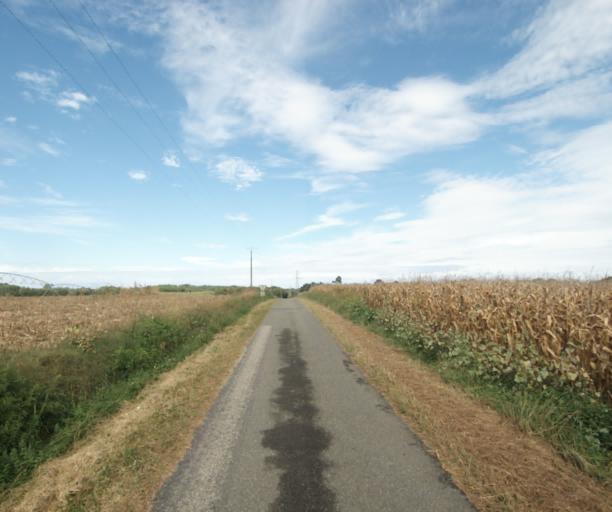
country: FR
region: Aquitaine
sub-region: Departement des Landes
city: Villeneuve-de-Marsan
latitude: 43.9011
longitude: -0.2257
